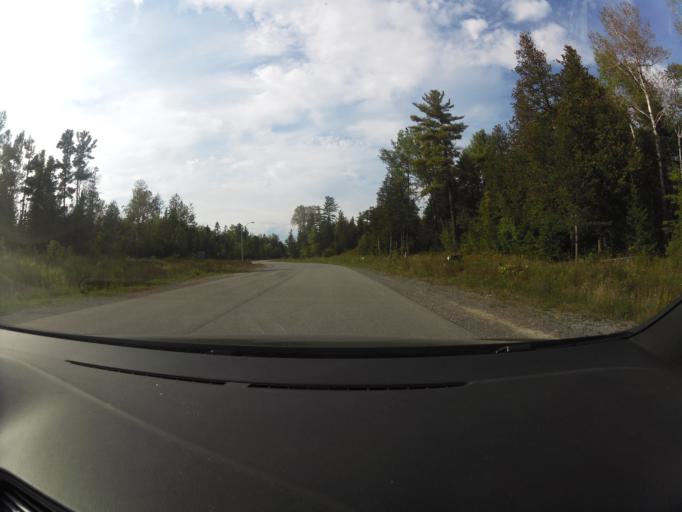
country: CA
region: Ontario
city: Carleton Place
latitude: 45.3378
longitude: -76.1563
